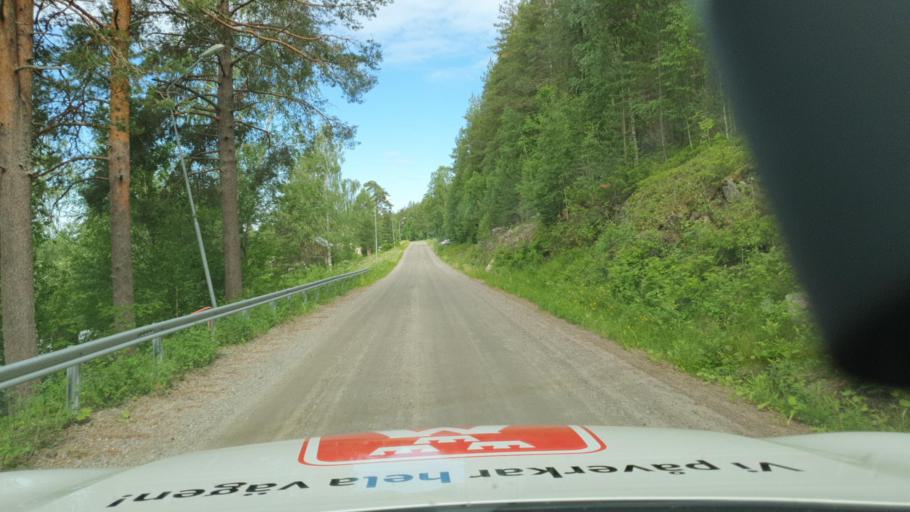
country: SE
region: Vaesterbotten
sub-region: Skelleftea Kommun
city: Forsbacka
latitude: 64.6559
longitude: 20.5376
